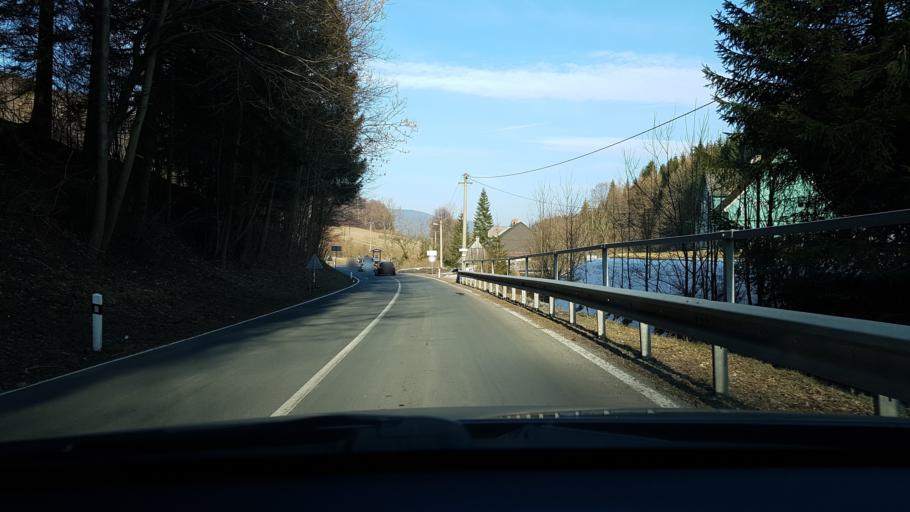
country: CZ
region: Olomoucky
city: Vapenna
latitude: 50.2099
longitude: 17.0929
